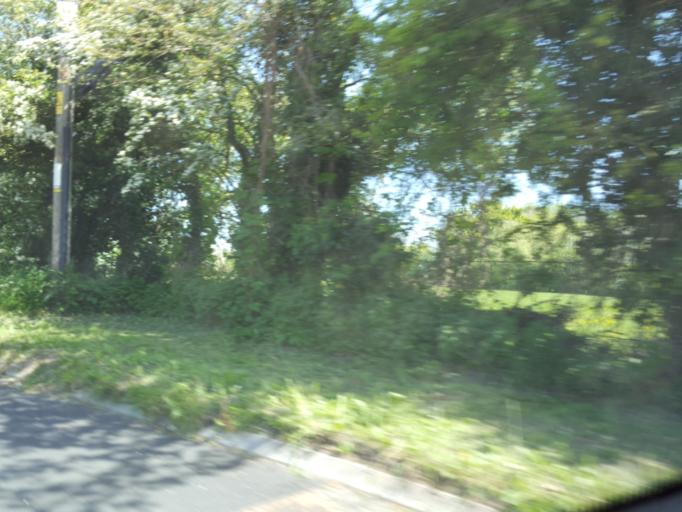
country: GB
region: England
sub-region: Wiltshire
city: Hankerton
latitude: 51.6301
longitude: -2.0722
